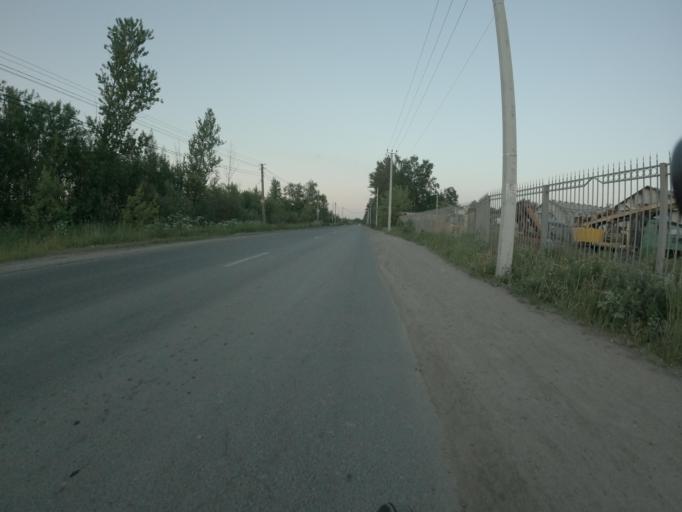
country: RU
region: St.-Petersburg
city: Dachnoye
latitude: 59.8228
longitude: 30.2851
